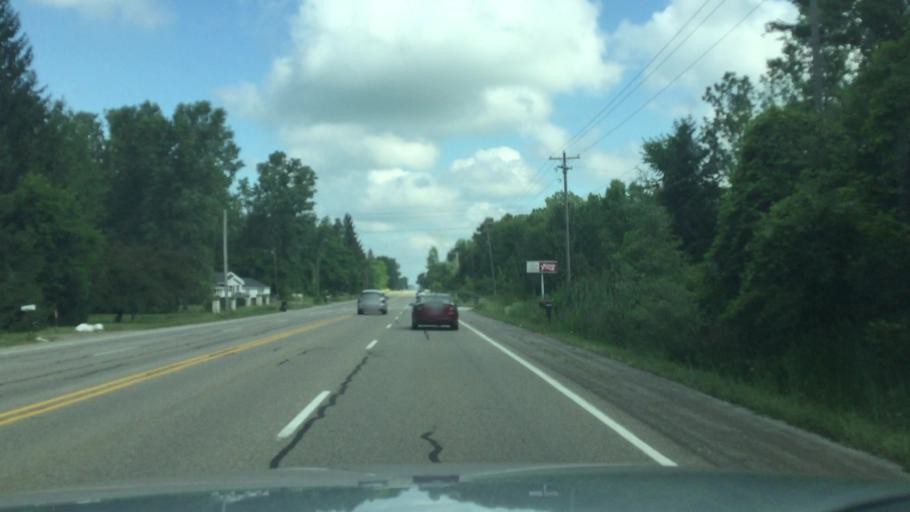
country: US
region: Michigan
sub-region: Genesee County
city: Clio
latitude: 43.2155
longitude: -83.7432
